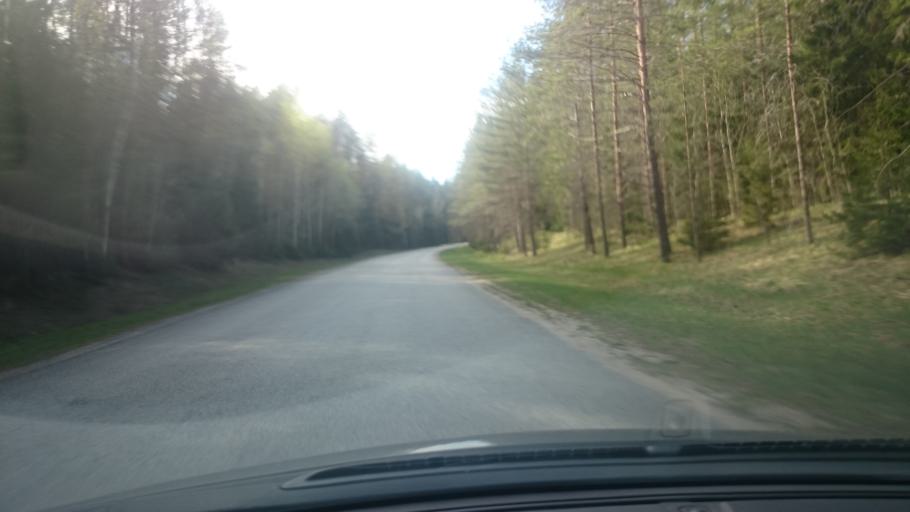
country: EE
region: Ida-Virumaa
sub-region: Toila vald
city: Voka
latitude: 59.1615
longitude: 27.5918
